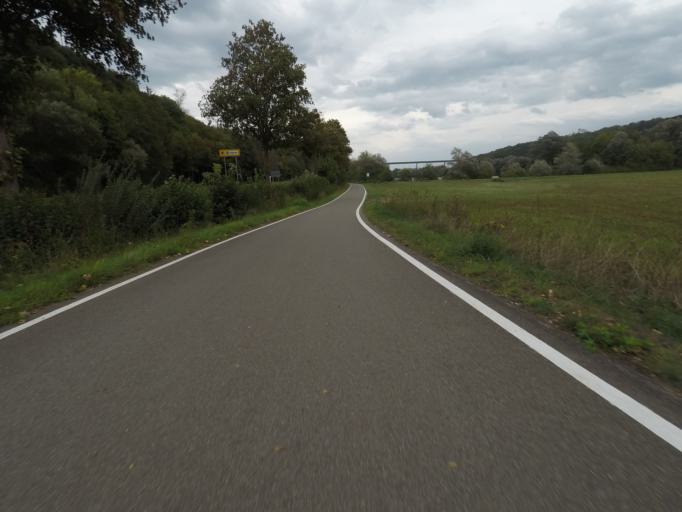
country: DE
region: Baden-Wuerttemberg
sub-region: Tuebingen Region
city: Kirchentellinsfurt
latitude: 48.5460
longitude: 9.1593
